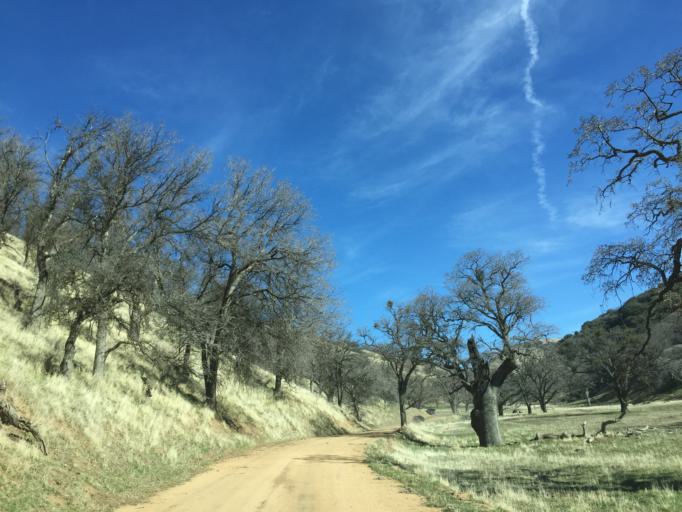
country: US
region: California
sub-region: Kern County
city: Lebec
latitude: 34.9070
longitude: -118.7117
